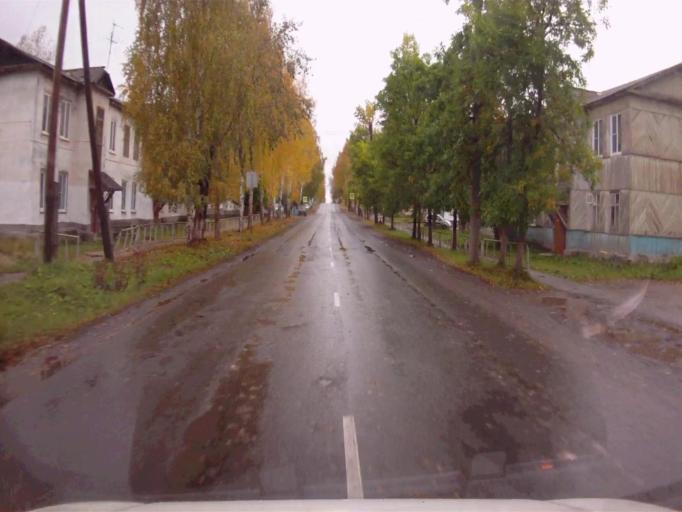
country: RU
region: Chelyabinsk
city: Verkhniy Ufaley
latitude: 56.0349
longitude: 60.2607
